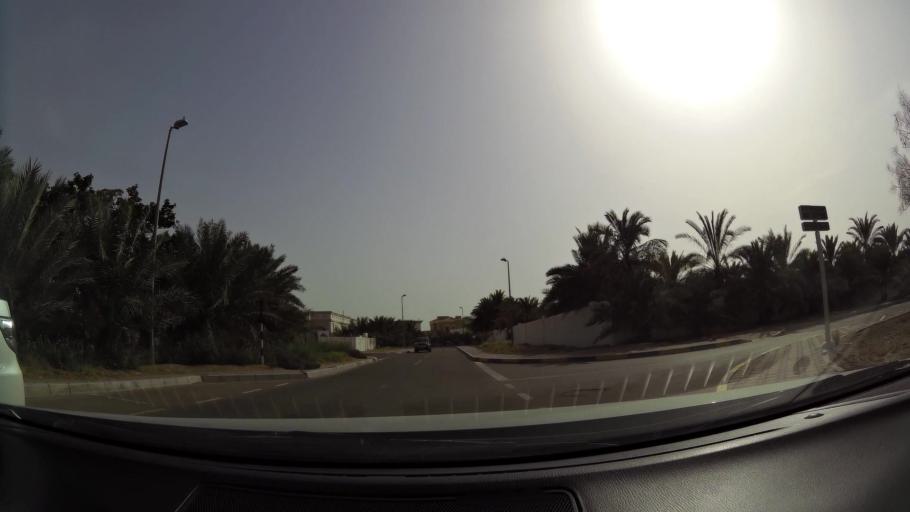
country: AE
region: Abu Dhabi
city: Al Ain
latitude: 24.1364
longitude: 55.7011
